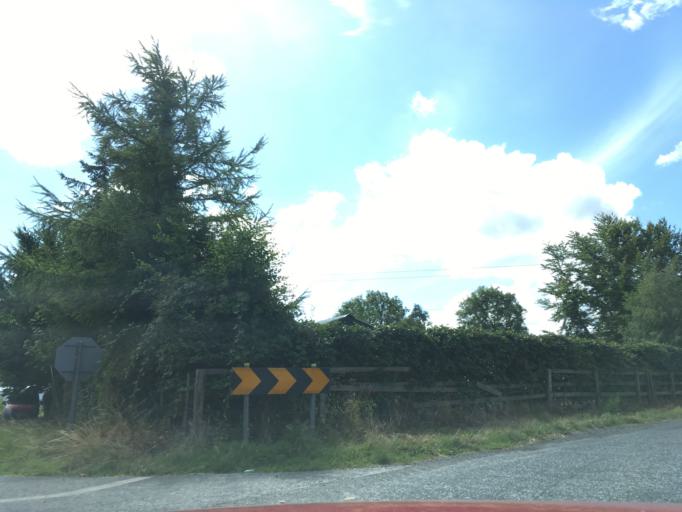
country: IE
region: Munster
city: Cahir
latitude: 52.3486
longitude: -7.9347
